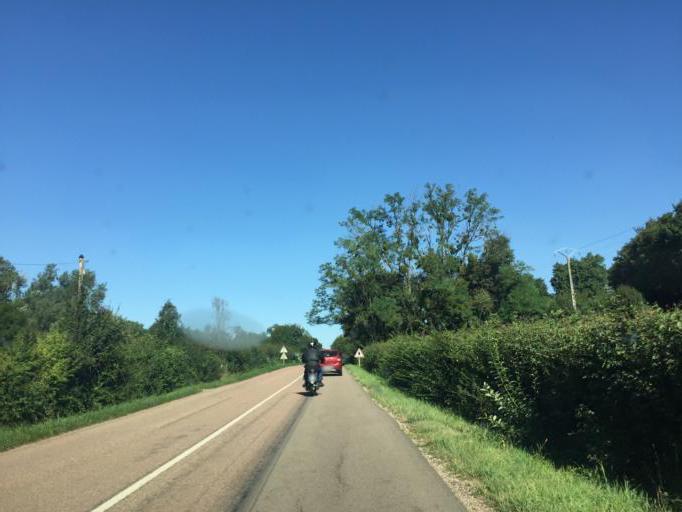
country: FR
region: Bourgogne
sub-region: Departement de la Nievre
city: Clamecy
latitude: 47.4700
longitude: 3.4460
